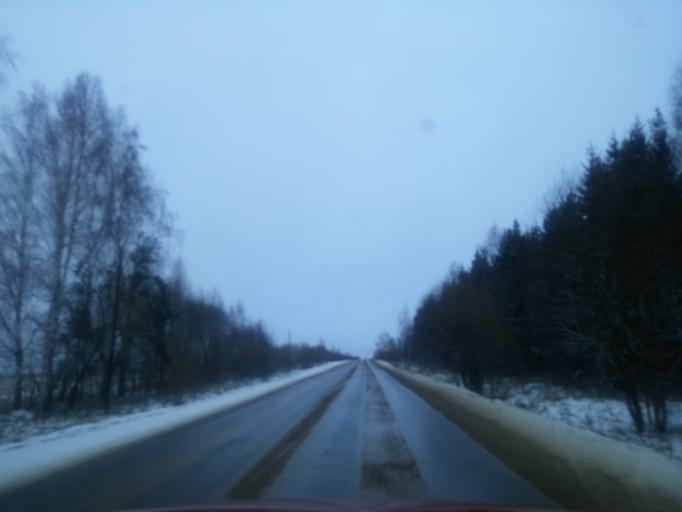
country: RU
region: Tverskaya
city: Likhoslavl'
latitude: 56.9584
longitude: 35.4288
